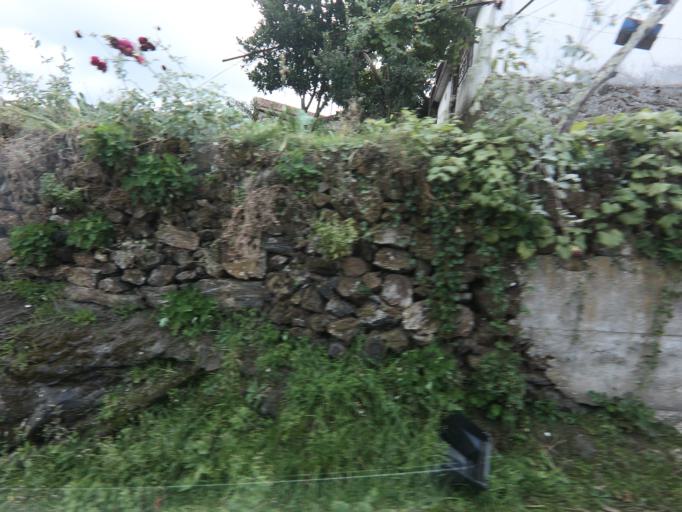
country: PT
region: Vila Real
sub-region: Mondim de Basto
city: Mondim de Basto
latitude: 41.3558
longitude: -7.8902
